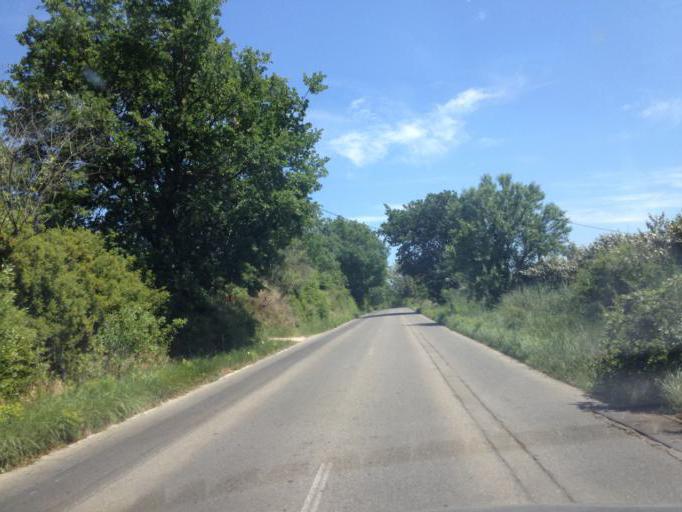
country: FR
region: Provence-Alpes-Cote d'Azur
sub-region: Departement du Vaucluse
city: Cadenet
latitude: 43.7379
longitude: 5.3533
